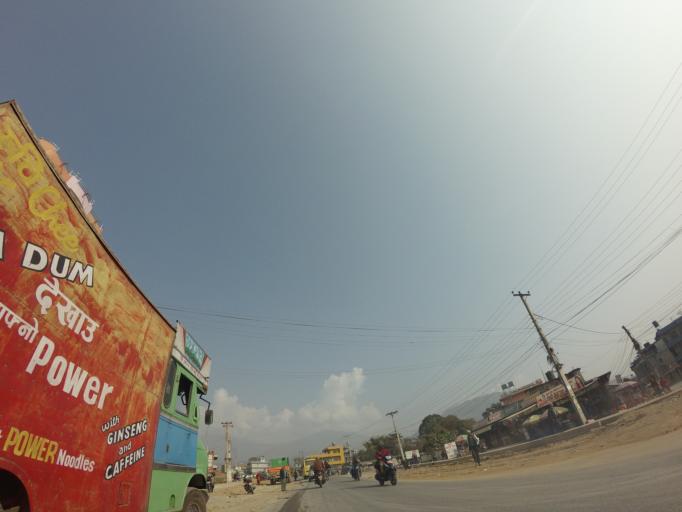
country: NP
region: Western Region
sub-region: Gandaki Zone
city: Pokhara
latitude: 28.2249
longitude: 83.9802
